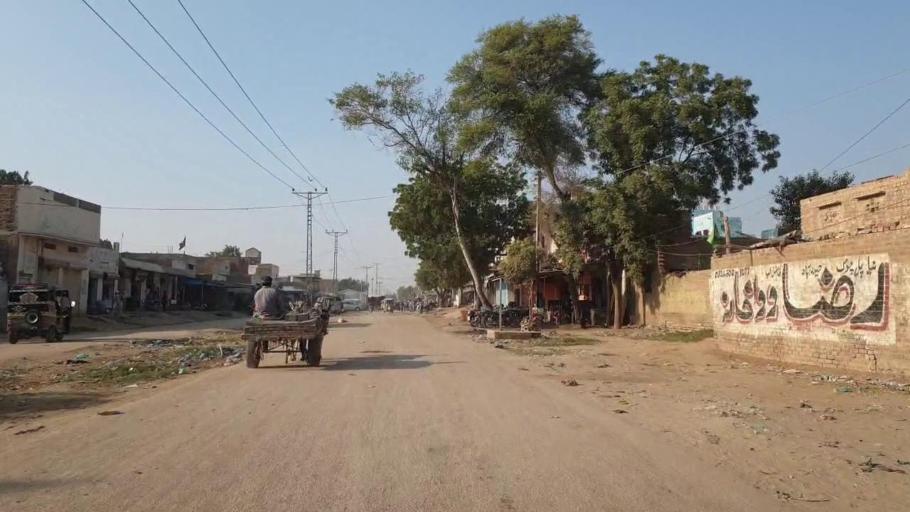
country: PK
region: Sindh
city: Kotri
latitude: 25.3564
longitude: 68.2567
